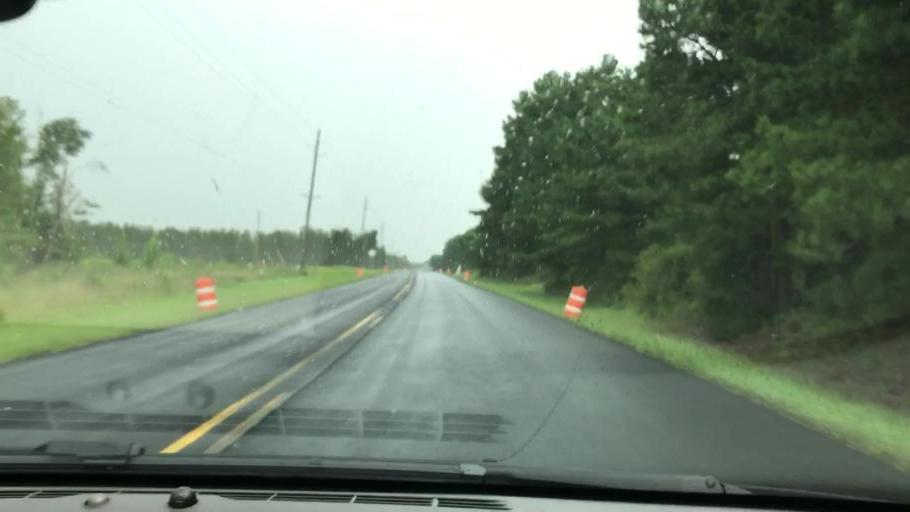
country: US
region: Georgia
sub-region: Clay County
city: Fort Gaines
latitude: 31.5302
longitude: -85.0220
